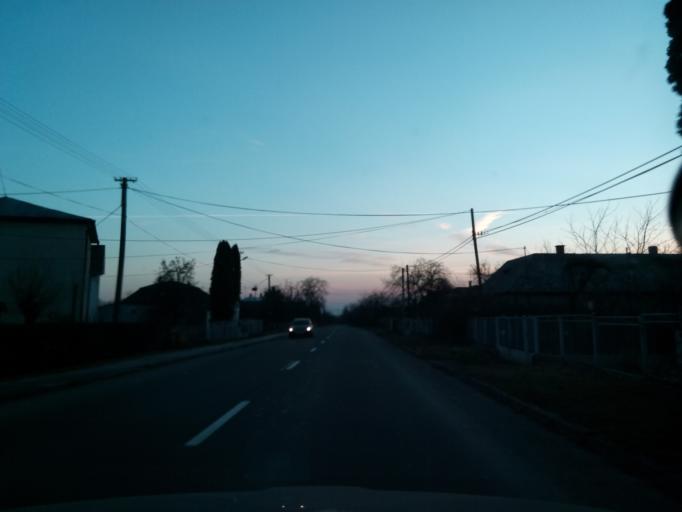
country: SK
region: Kosicky
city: Sobrance
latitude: 48.7897
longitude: 22.1368
